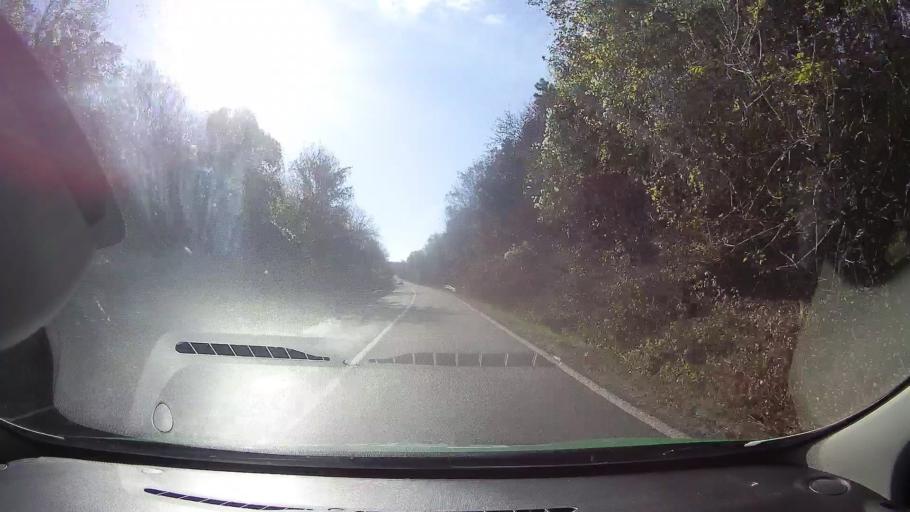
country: RO
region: Tulcea
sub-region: Oras Babadag
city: Babadag
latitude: 44.8390
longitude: 28.6960
